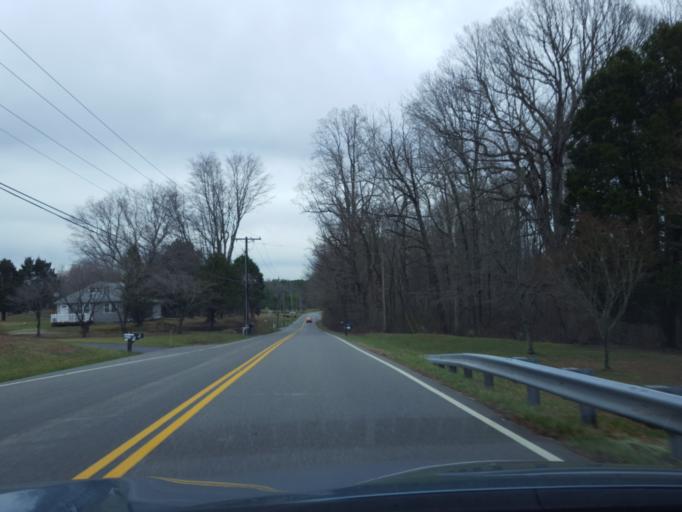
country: US
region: Maryland
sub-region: Calvert County
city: Huntingtown
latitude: 38.6273
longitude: -76.5931
